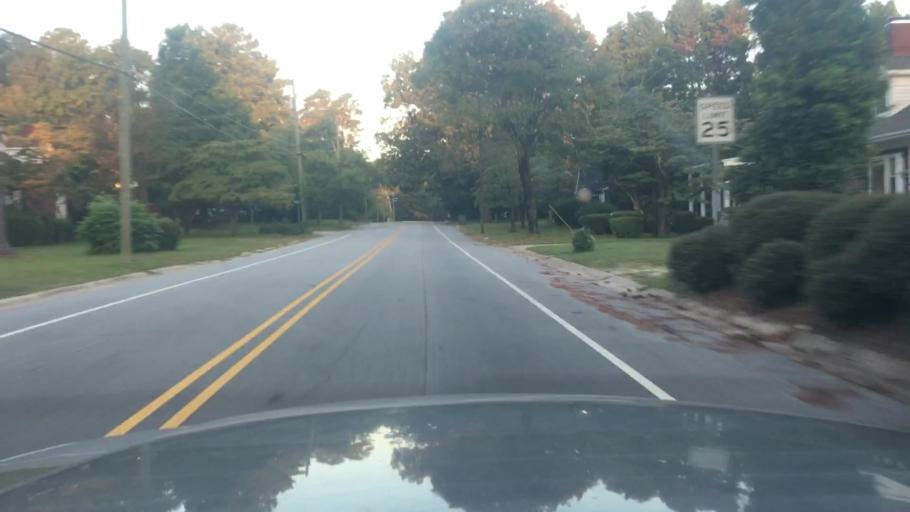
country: US
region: North Carolina
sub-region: Cumberland County
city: Fayetteville
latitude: 35.0857
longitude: -78.8769
